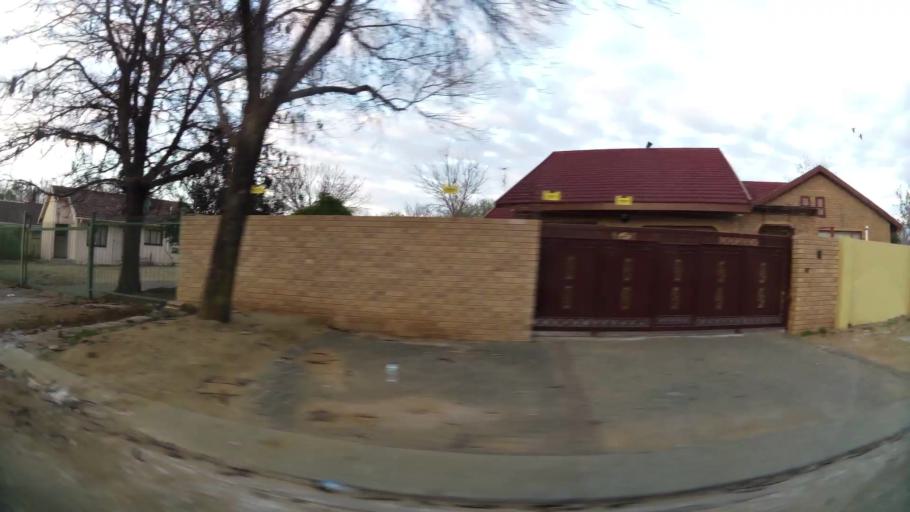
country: ZA
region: Orange Free State
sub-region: Mangaung Metropolitan Municipality
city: Bloemfontein
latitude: -29.1724
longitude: 26.1875
